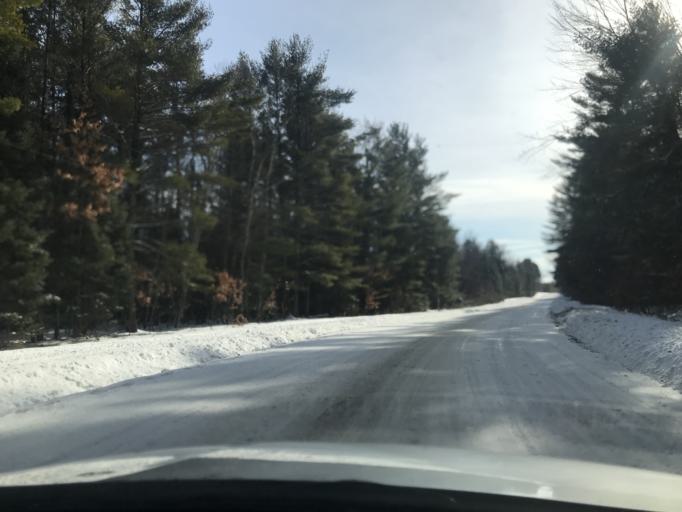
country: US
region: Wisconsin
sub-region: Oconto County
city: Gillett
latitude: 45.1361
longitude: -88.2498
